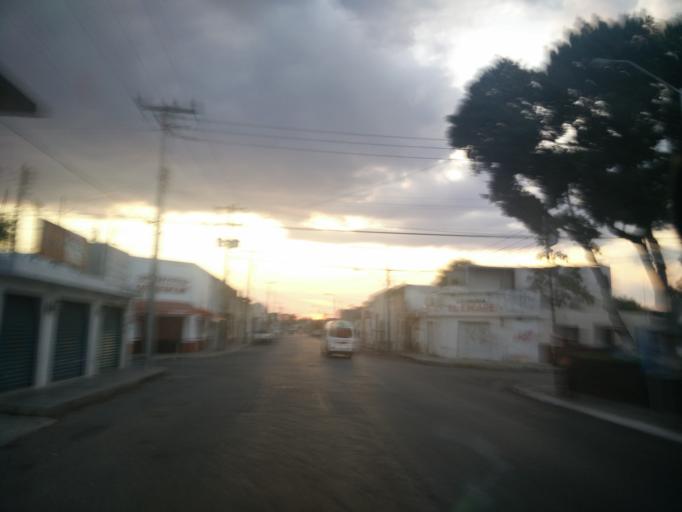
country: MX
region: Yucatan
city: Merida
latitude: 20.9634
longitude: -89.6332
